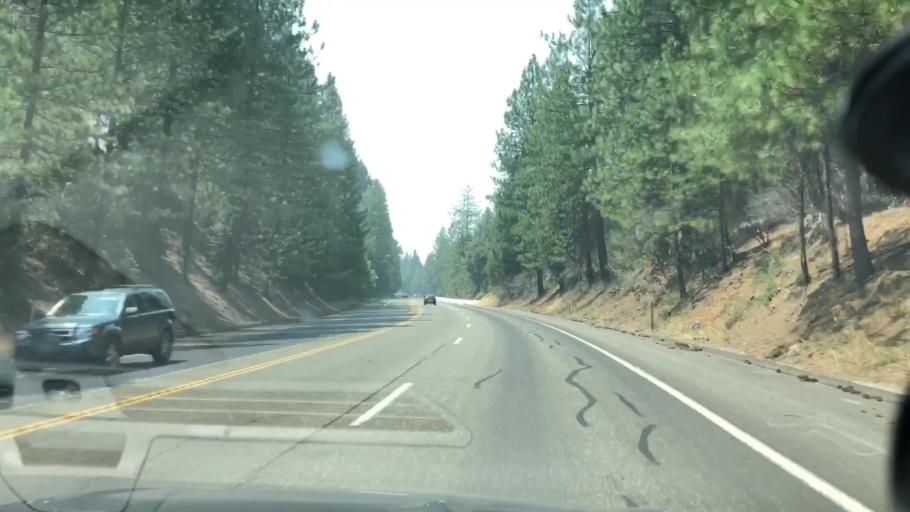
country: US
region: California
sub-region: El Dorado County
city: Pollock Pines
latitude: 38.7618
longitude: -120.5340
